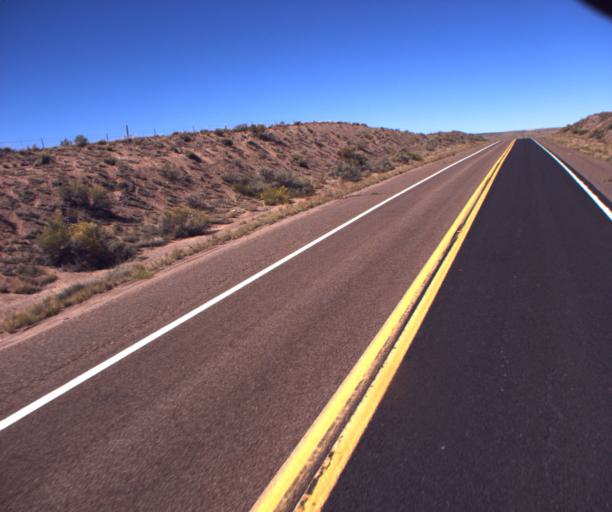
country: US
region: Arizona
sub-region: Navajo County
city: Snowflake
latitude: 34.7508
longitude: -109.8020
